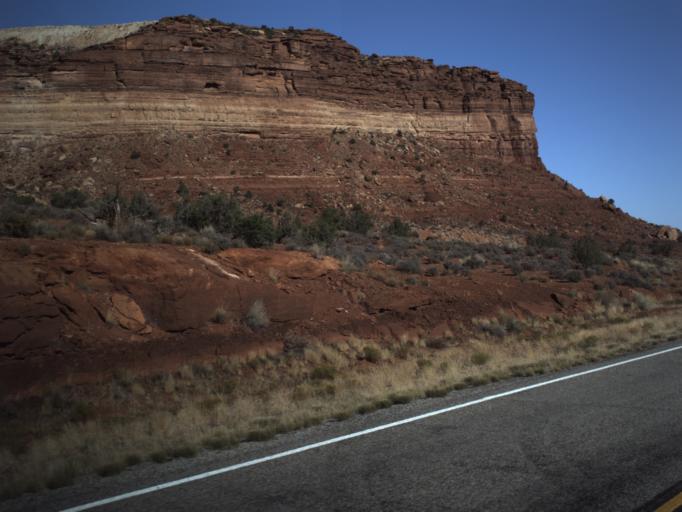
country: US
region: Utah
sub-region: San Juan County
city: Blanding
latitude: 37.7481
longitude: -110.2804
